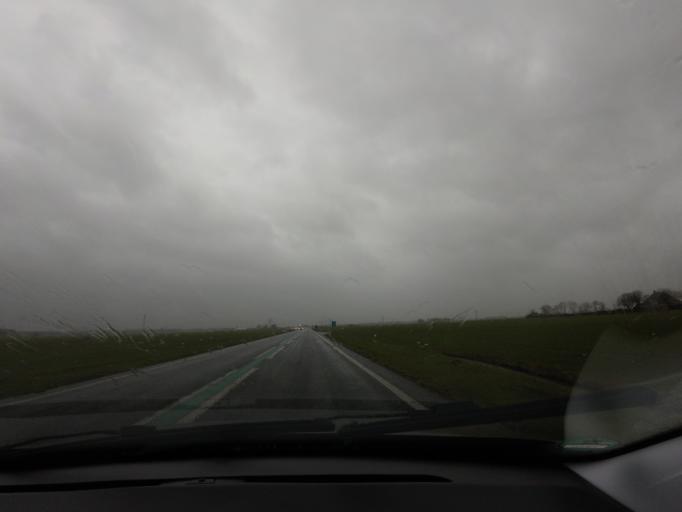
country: NL
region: Friesland
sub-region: Sudwest Fryslan
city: Bolsward
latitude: 53.0813
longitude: 5.5187
